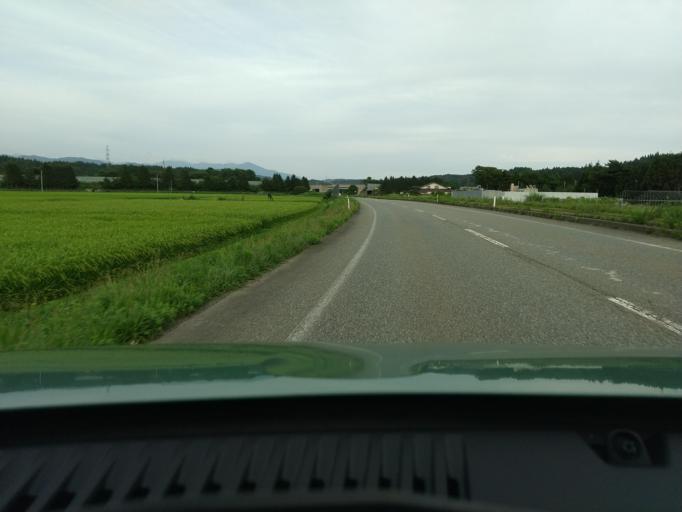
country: JP
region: Akita
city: Akita Shi
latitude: 39.7948
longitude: 140.0980
